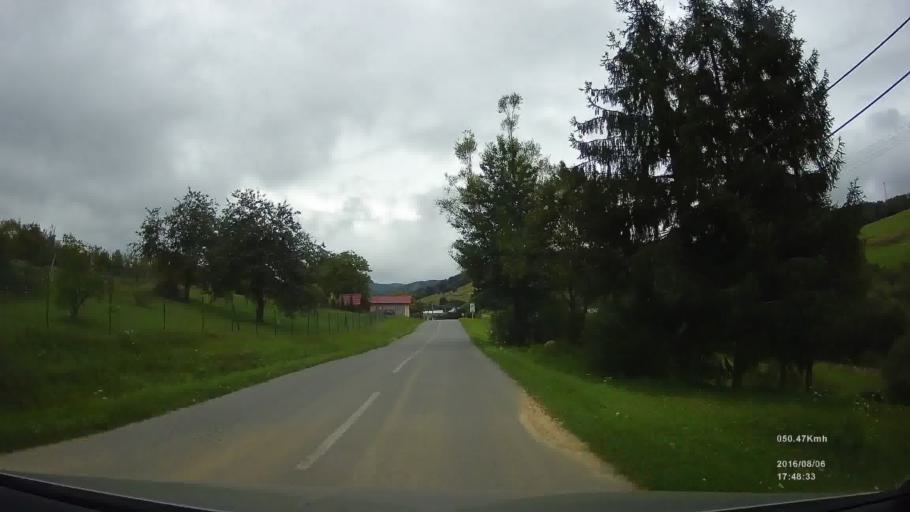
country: SK
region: Presovsky
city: Svidnik
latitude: 49.3776
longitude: 21.5729
